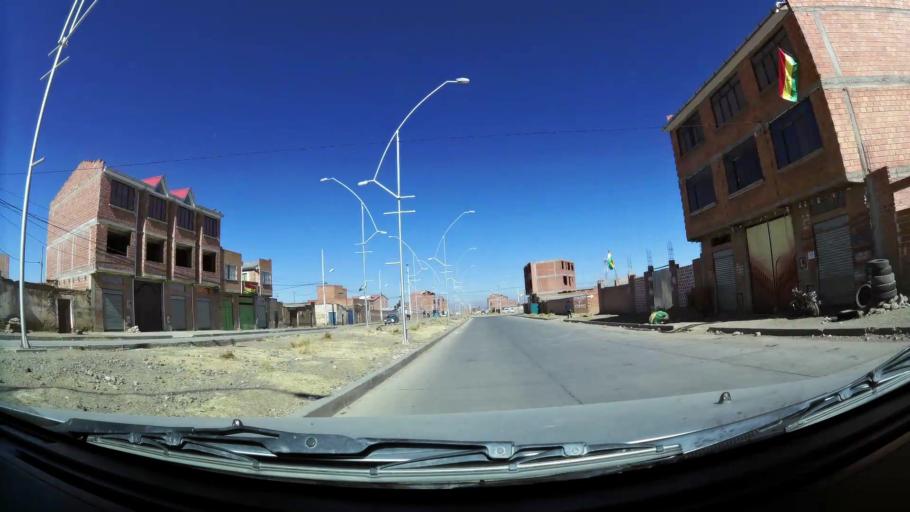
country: BO
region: La Paz
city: La Paz
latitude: -16.5331
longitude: -68.2255
